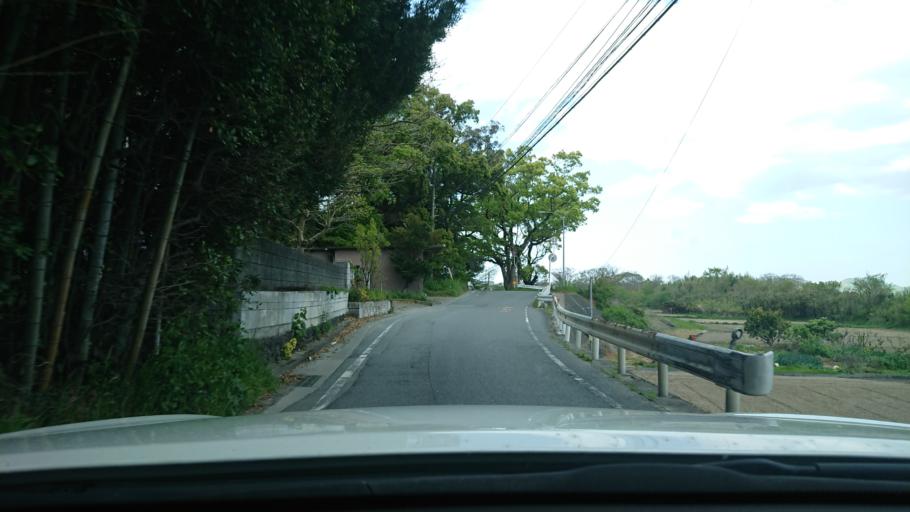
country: JP
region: Tokushima
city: Komatsushimacho
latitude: 33.9874
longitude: 134.5451
